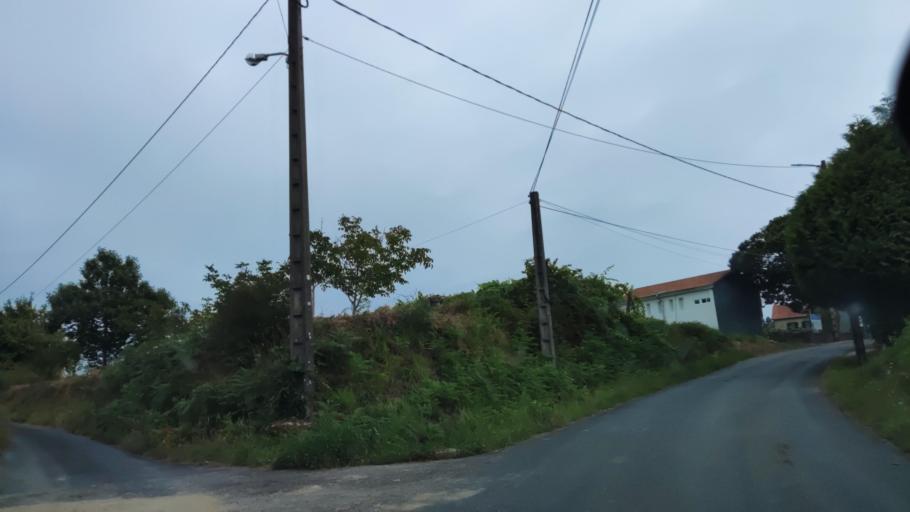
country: ES
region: Galicia
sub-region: Provincia da Coruna
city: Padron
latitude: 42.7187
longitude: -8.6876
